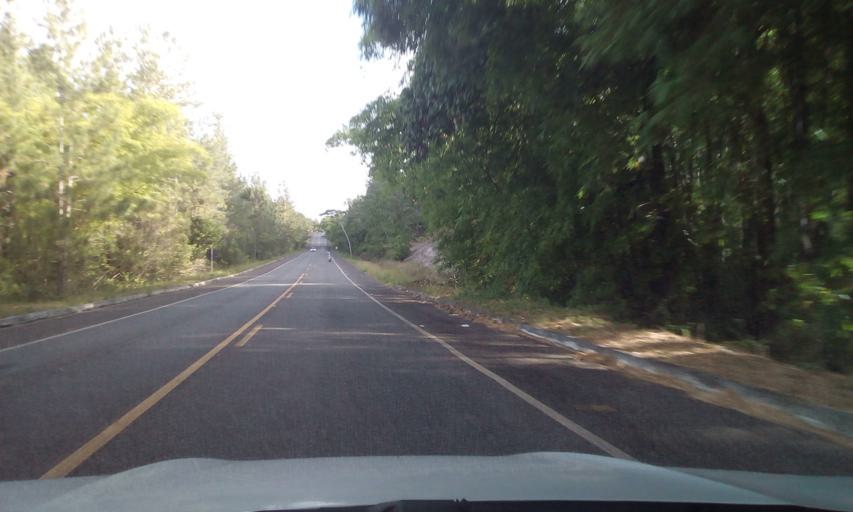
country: BR
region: Bahia
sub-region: Entre Rios
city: Entre Rios
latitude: -12.1188
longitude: -37.7879
